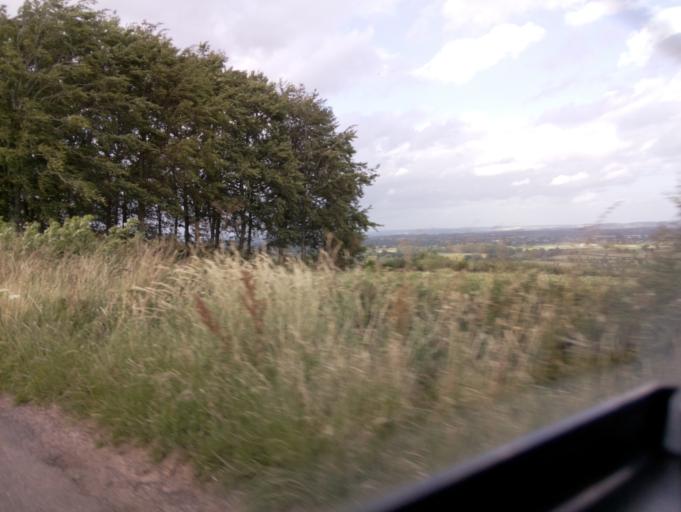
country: GB
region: England
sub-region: Gloucestershire
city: Donnington
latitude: 51.9686
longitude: -1.7512
